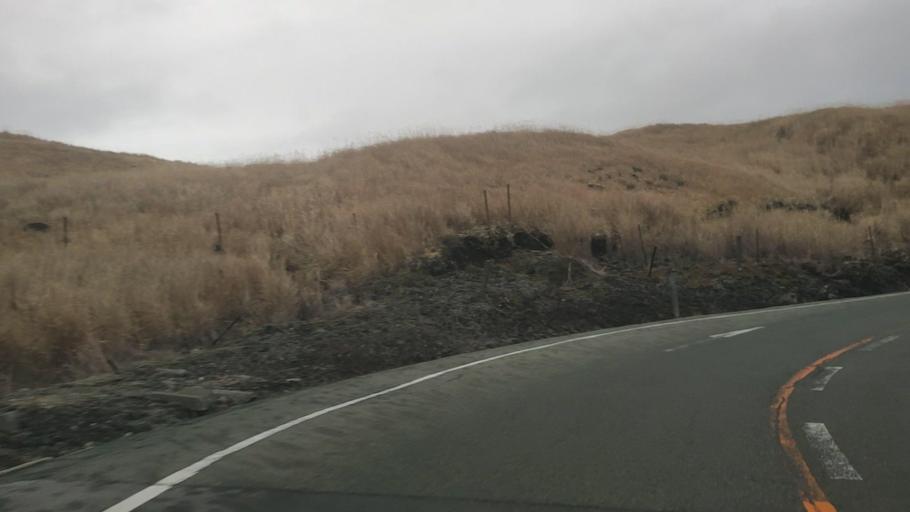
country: JP
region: Kumamoto
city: Aso
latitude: 32.9050
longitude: 131.0363
